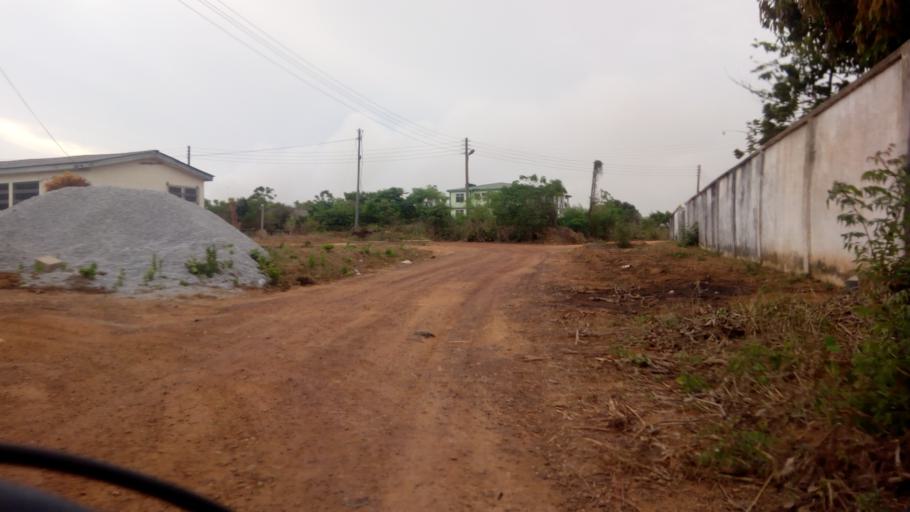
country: GH
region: Central
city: Cape Coast
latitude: 5.1092
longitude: -1.2748
